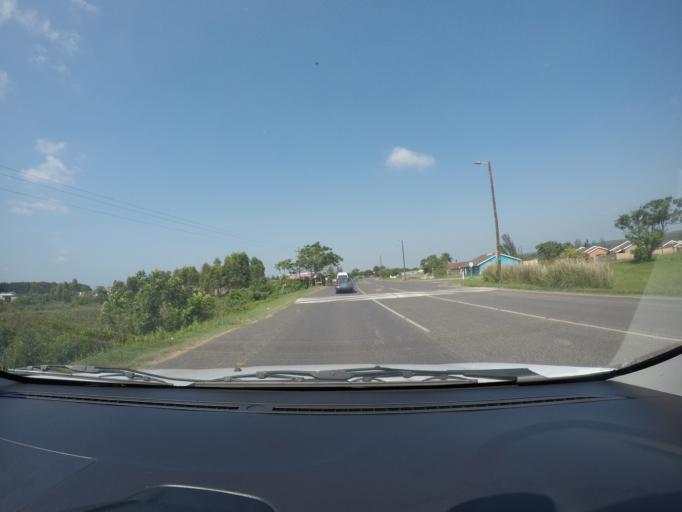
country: ZA
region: KwaZulu-Natal
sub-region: uThungulu District Municipality
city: eSikhawini
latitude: -28.8919
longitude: 31.8903
